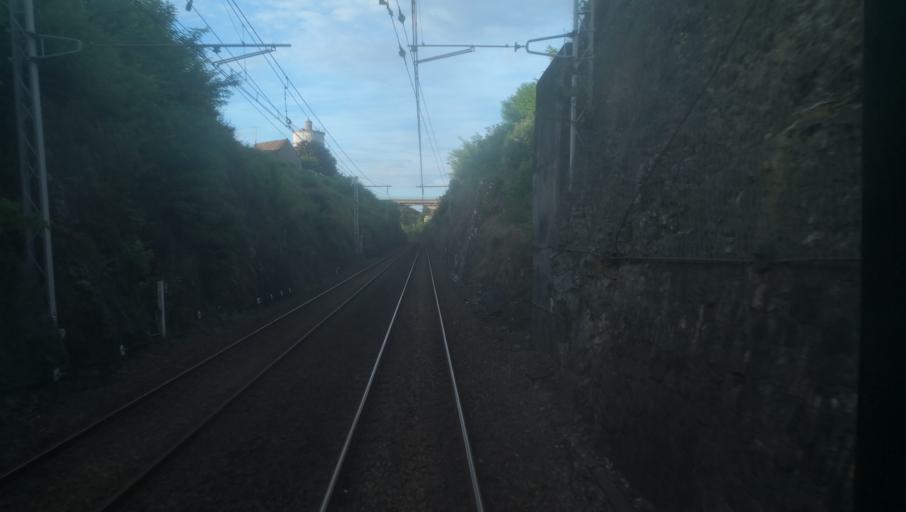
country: FR
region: Centre
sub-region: Departement de l'Indre
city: Saint-Marcel
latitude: 46.6226
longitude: 1.5026
